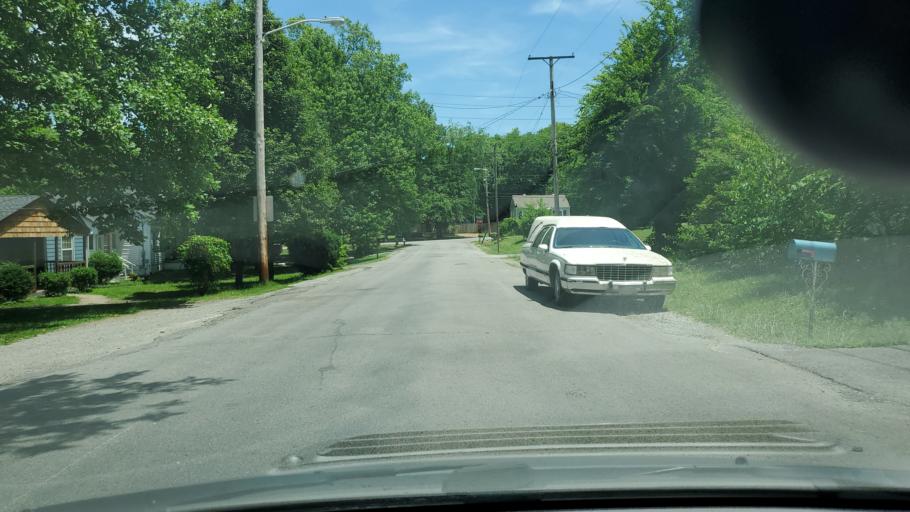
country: US
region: Tennessee
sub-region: Davidson County
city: Nashville
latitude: 36.2061
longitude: -86.7535
